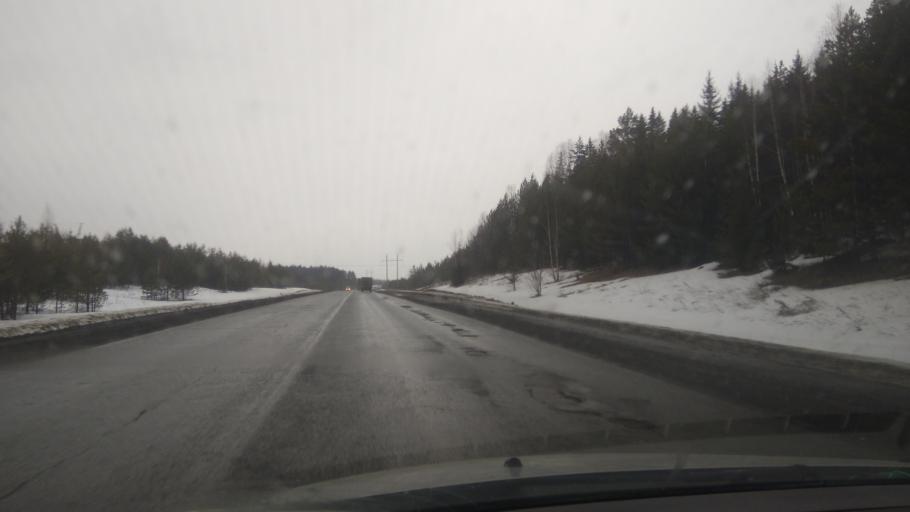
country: RU
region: Perm
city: Kungur
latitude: 57.3319
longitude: 56.9523
